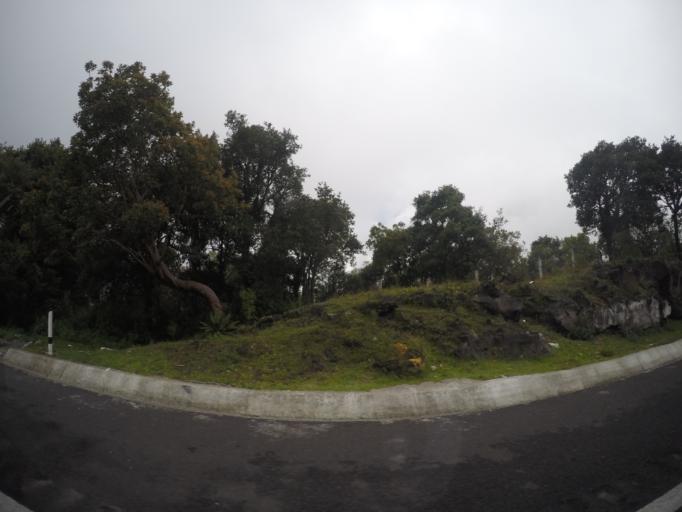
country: MX
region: Morelos
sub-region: Cuernavaca
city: Villa Santiago
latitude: 19.0271
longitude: -99.1978
